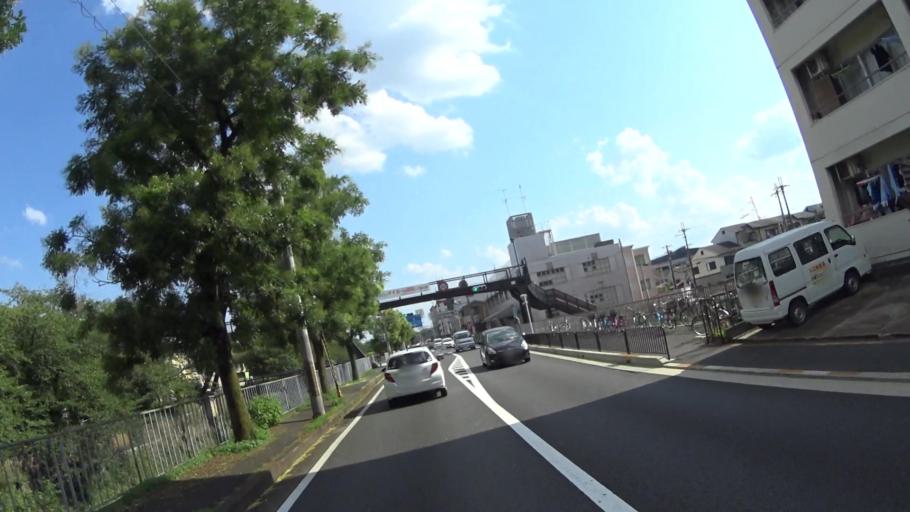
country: JP
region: Kyoto
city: Muko
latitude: 34.9983
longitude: 135.7167
